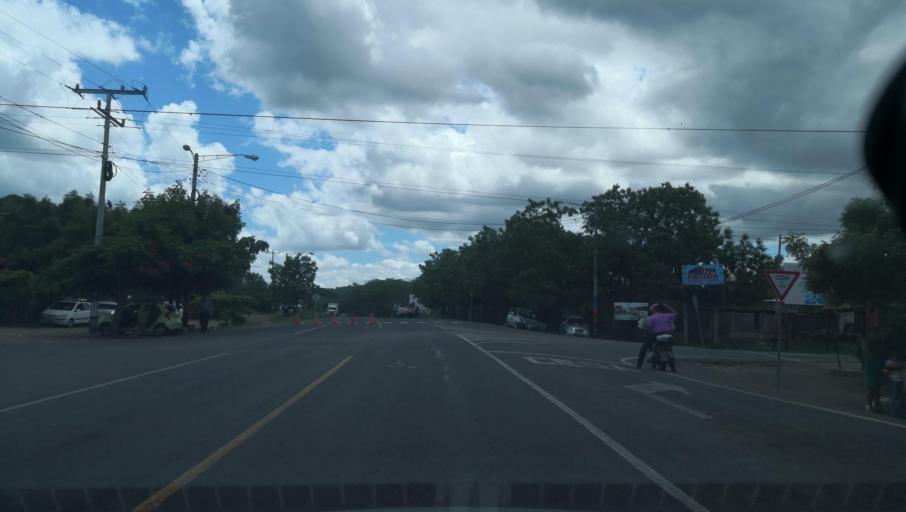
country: NI
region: Madriz
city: Palacaguina
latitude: 13.4326
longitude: -86.4106
